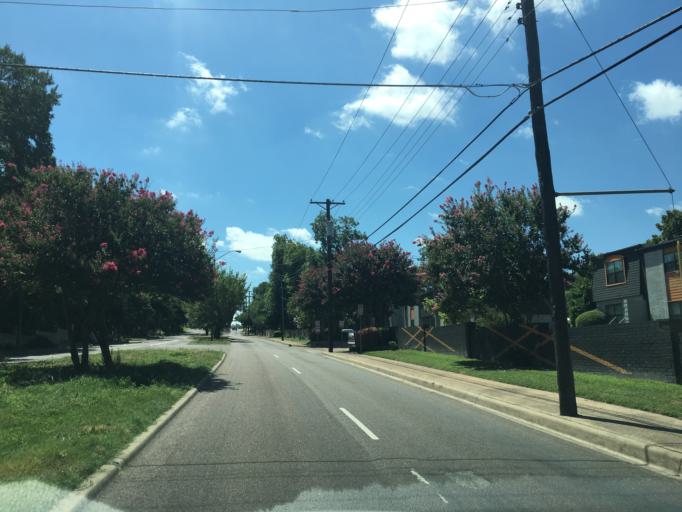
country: US
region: Texas
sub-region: Dallas County
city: Garland
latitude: 32.8455
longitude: -96.6939
